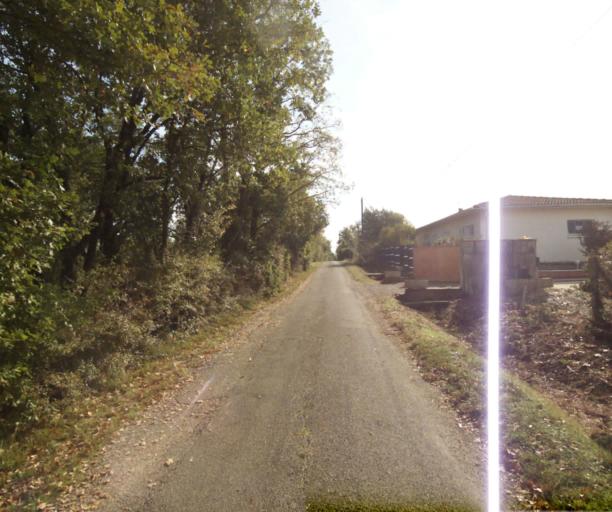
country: FR
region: Midi-Pyrenees
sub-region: Departement du Tarn-et-Garonne
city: Orgueil
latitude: 43.9000
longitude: 1.4152
